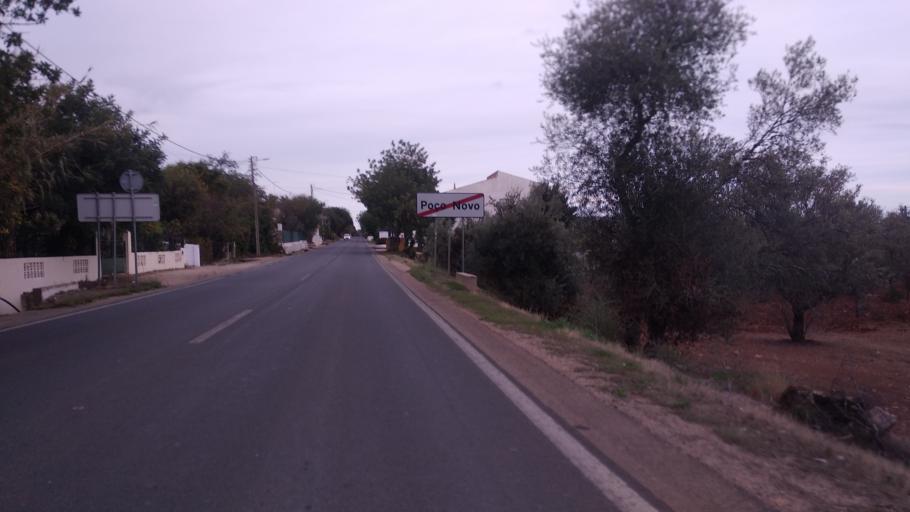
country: PT
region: Faro
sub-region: Faro
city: Santa Barbara de Nexe
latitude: 37.1467
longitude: -7.9701
